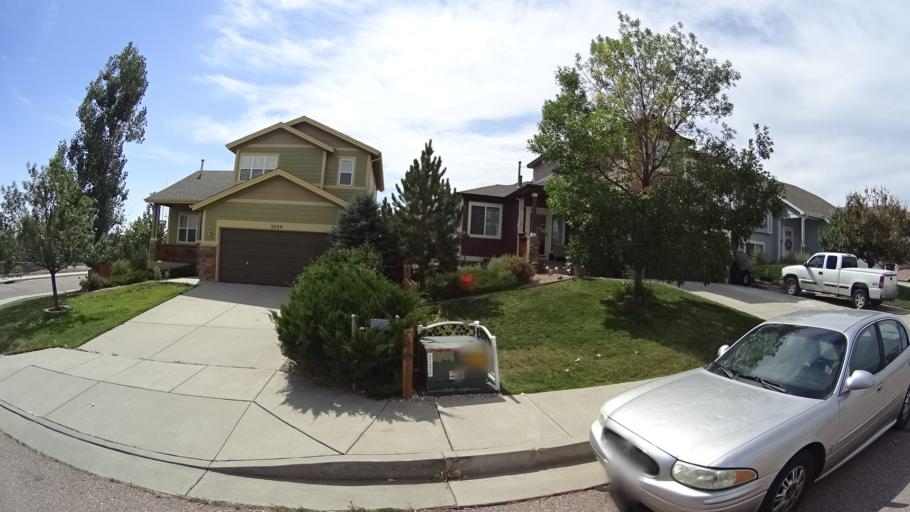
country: US
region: Colorado
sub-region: El Paso County
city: Cimarron Hills
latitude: 38.9077
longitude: -104.7084
